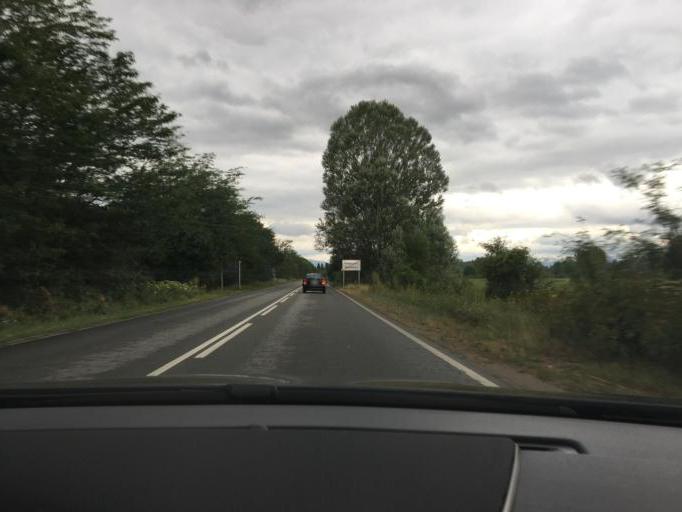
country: BG
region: Kyustendil
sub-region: Obshtina Kyustendil
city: Kyustendil
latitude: 42.2579
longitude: 22.8399
